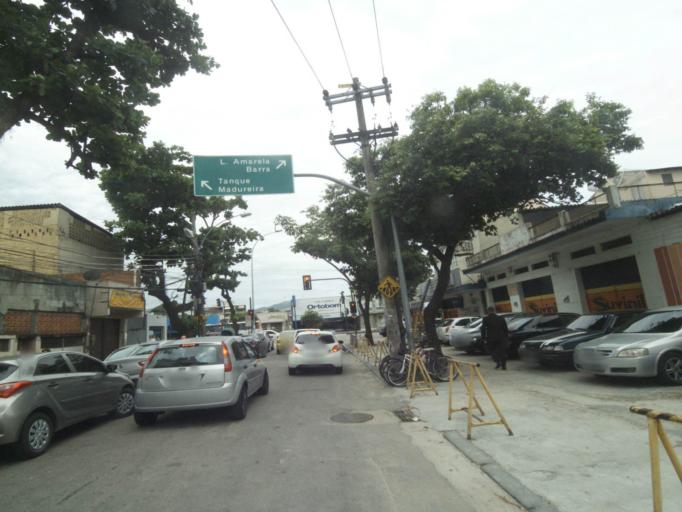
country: BR
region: Rio de Janeiro
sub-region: Sao Joao De Meriti
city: Sao Joao de Meriti
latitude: -22.9266
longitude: -43.3742
